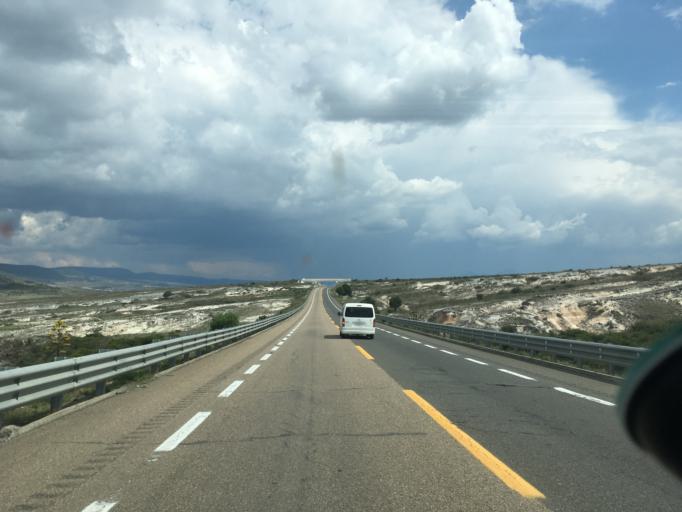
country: MX
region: Oaxaca
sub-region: Villa Tejupam de la Union
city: Villa Tejupam de la Union
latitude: 17.8167
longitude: -97.3679
